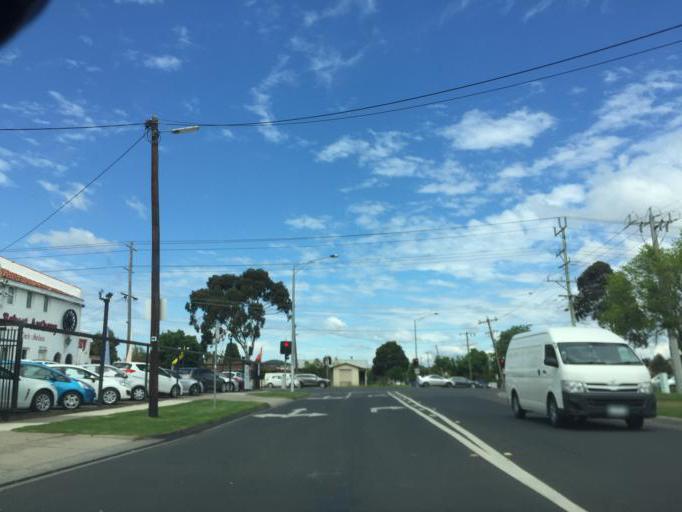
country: AU
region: Victoria
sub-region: Maribyrnong
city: Braybrook
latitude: -37.7789
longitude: 144.8523
